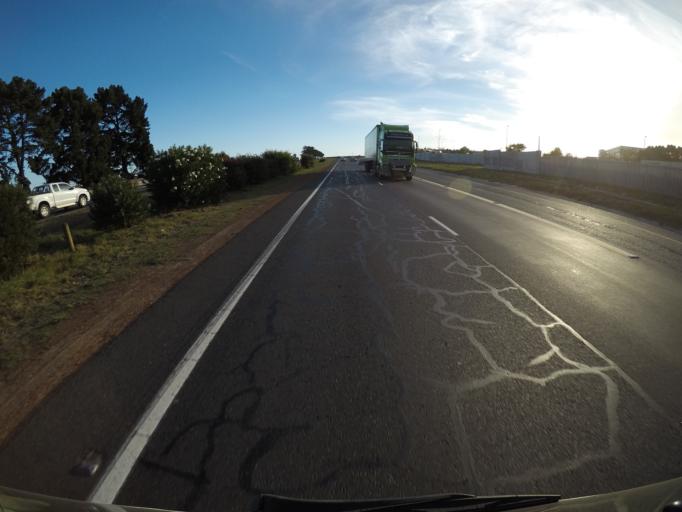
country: ZA
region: Western Cape
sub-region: City of Cape Town
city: Kraaifontein
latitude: -33.8550
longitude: 18.6999
